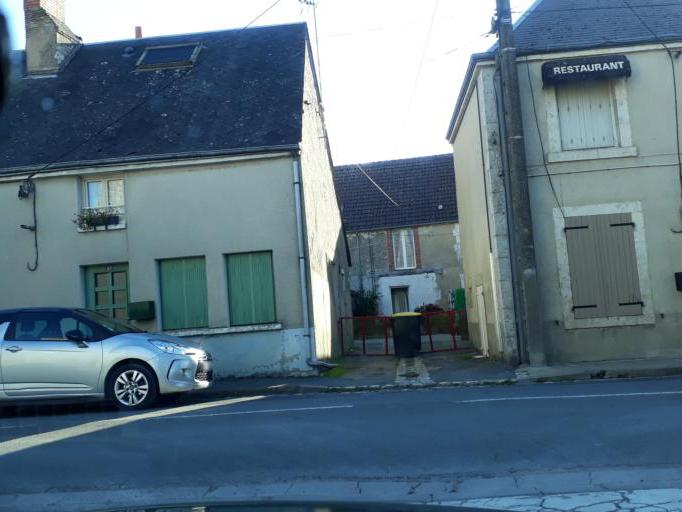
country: FR
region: Centre
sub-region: Departement du Loiret
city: Beaugency
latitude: 47.8286
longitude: 1.5730
